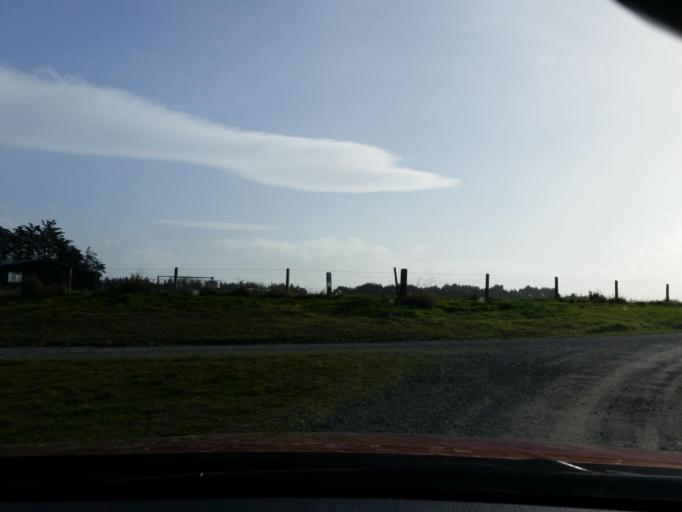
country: NZ
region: Southland
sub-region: Invercargill City
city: Invercargill
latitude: -46.2806
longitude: 168.4155
